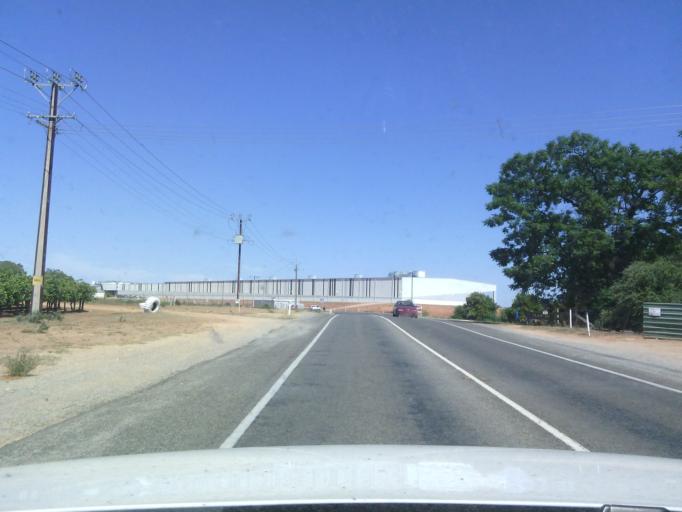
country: AU
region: South Australia
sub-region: Berri and Barmera
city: Monash
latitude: -34.2766
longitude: 140.5363
